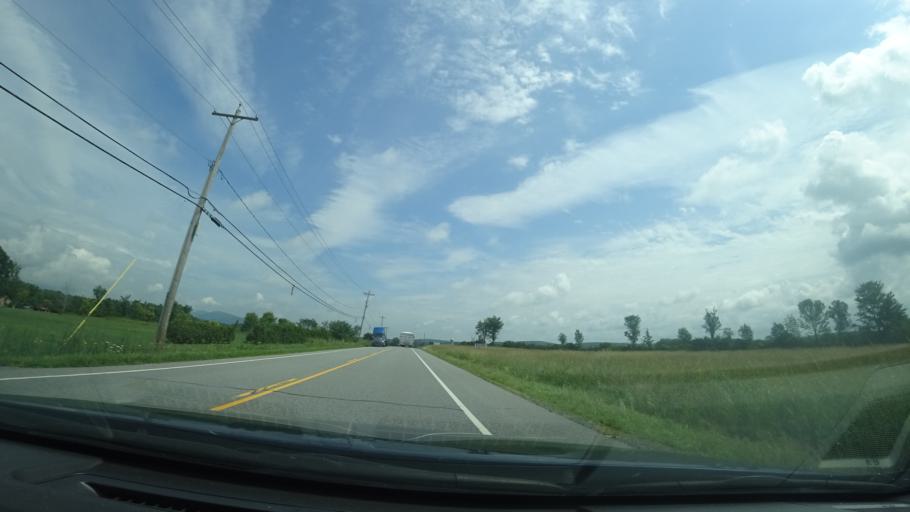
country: US
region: New York
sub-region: Warren County
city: Queensbury
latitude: 43.3817
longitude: -73.5056
